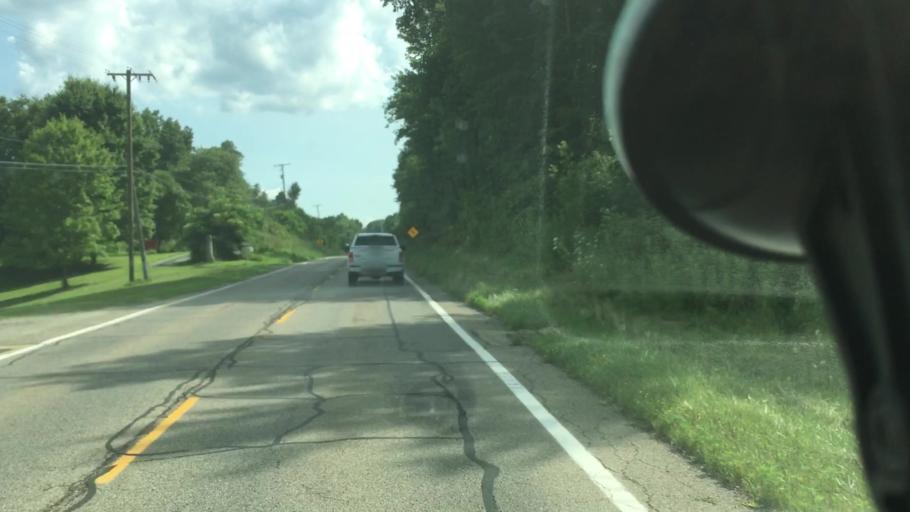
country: US
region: Ohio
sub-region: Columbiana County
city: Salem
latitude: 40.9474
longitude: -80.8357
